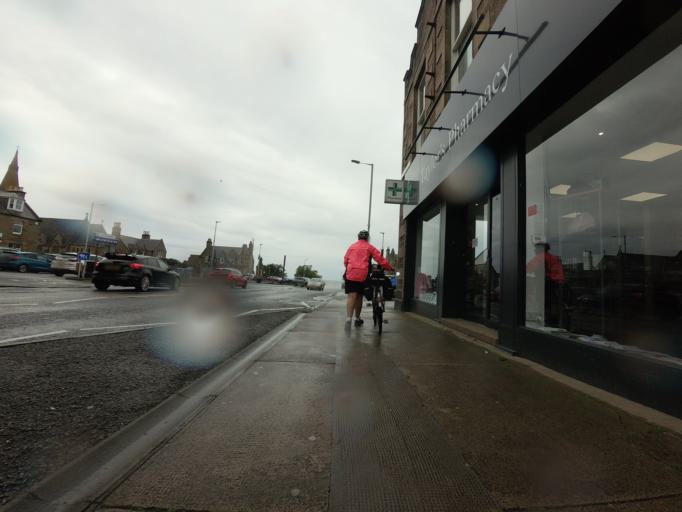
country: GB
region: Scotland
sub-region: Moray
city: Buckie
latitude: 57.6759
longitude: -2.9645
